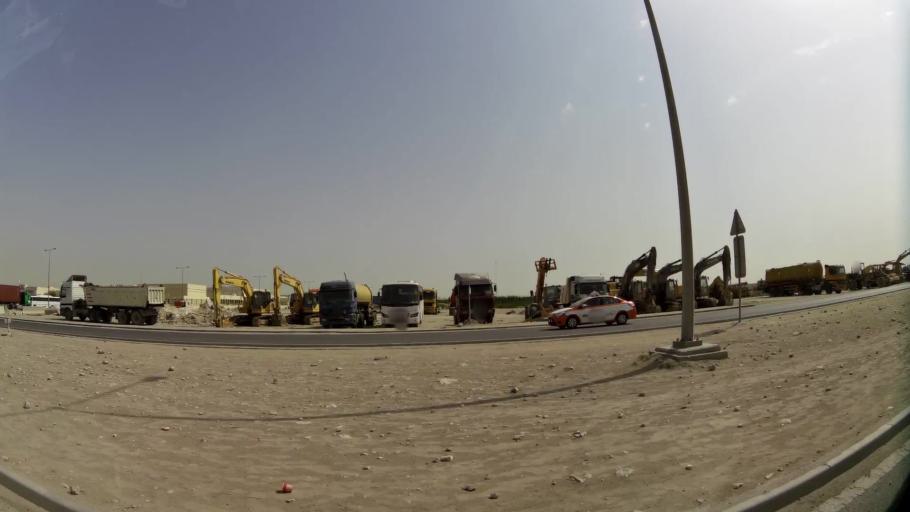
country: QA
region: Al Wakrah
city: Al Wukayr
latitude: 25.1821
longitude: 51.4625
